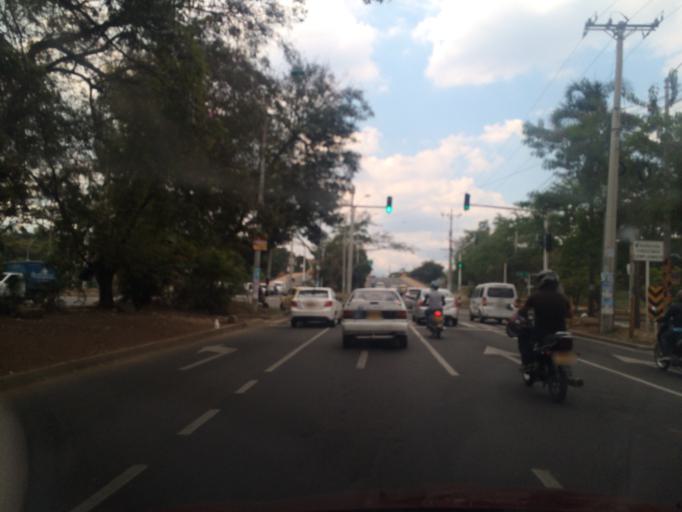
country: CO
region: Valle del Cauca
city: Cali
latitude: 3.3854
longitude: -76.5285
